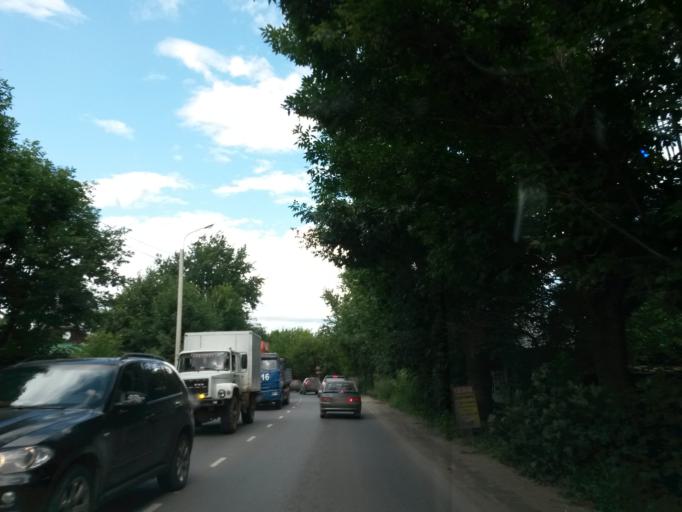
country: RU
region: Ivanovo
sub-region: Gorod Ivanovo
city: Ivanovo
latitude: 56.9925
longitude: 40.9528
